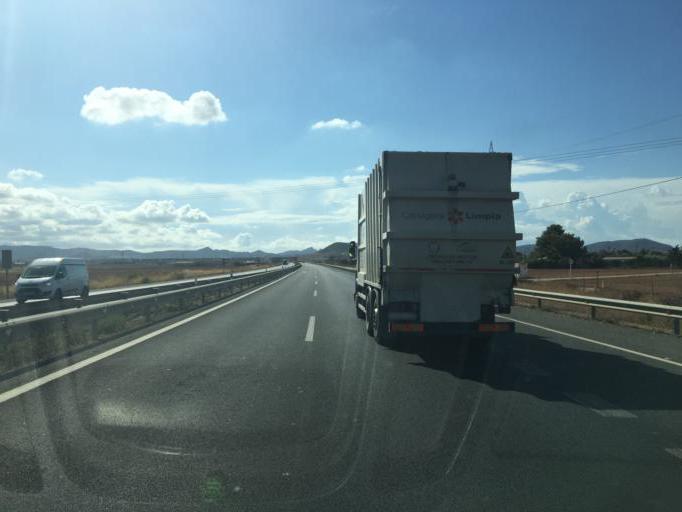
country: ES
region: Murcia
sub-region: Murcia
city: Cartagena
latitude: 37.6536
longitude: -0.9777
